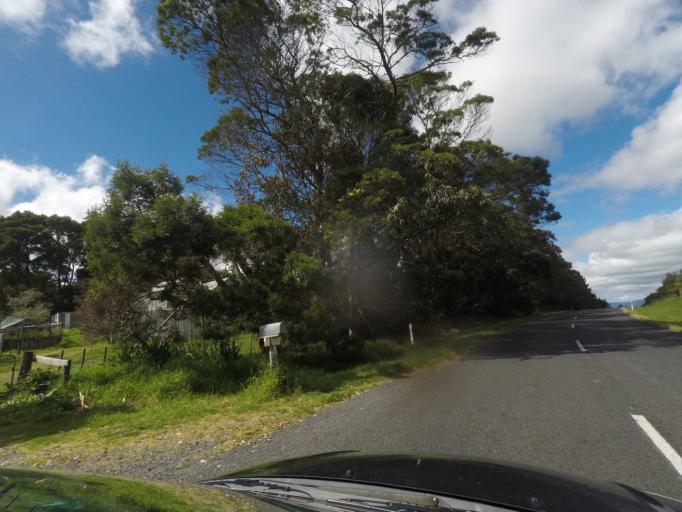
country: NZ
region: Auckland
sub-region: Auckland
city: Rothesay Bay
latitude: -36.7594
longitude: 174.6494
